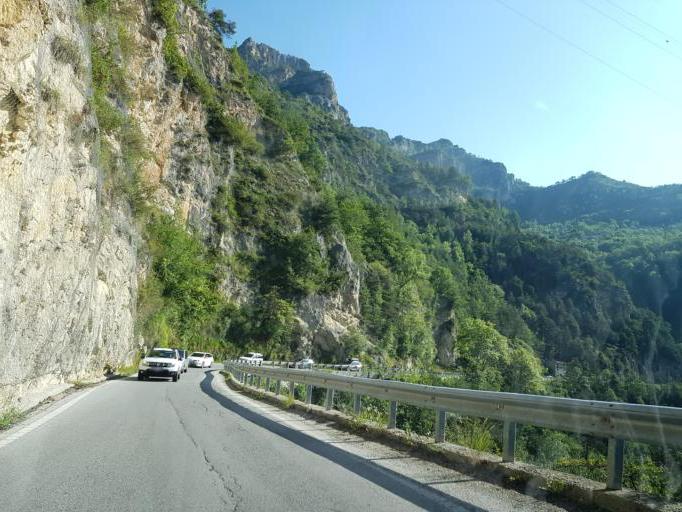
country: IT
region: Piedmont
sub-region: Provincia di Cuneo
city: Macra
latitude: 44.4990
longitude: 7.1878
